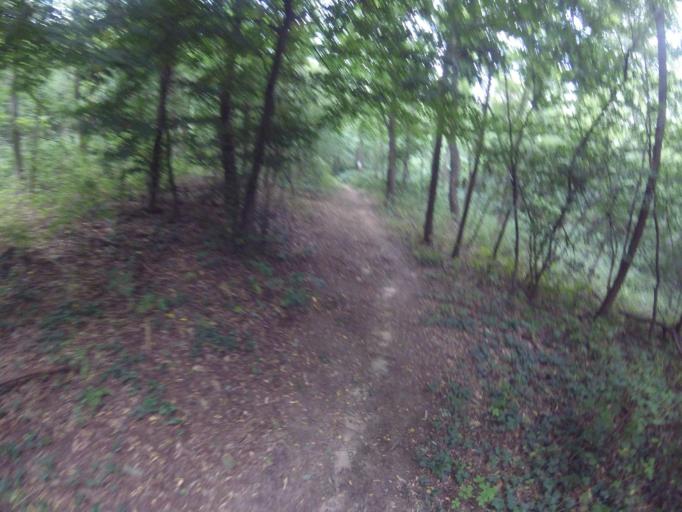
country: HU
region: Veszprem
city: Badacsonytomaj
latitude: 46.8301
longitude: 17.5083
